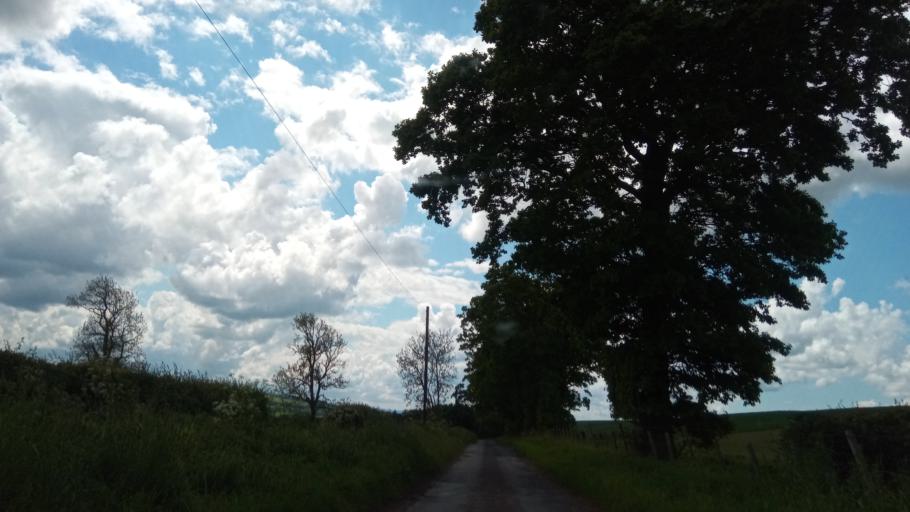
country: GB
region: Scotland
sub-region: The Scottish Borders
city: Coldstream
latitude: 55.5765
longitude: -2.3196
